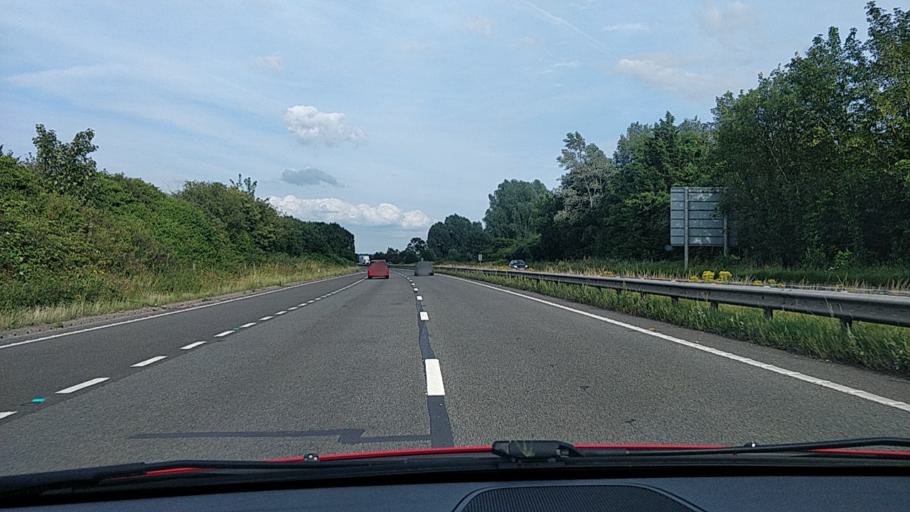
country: GB
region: Wales
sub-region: County of Flintshire
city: Hawarden
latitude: 53.1603
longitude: -3.0013
